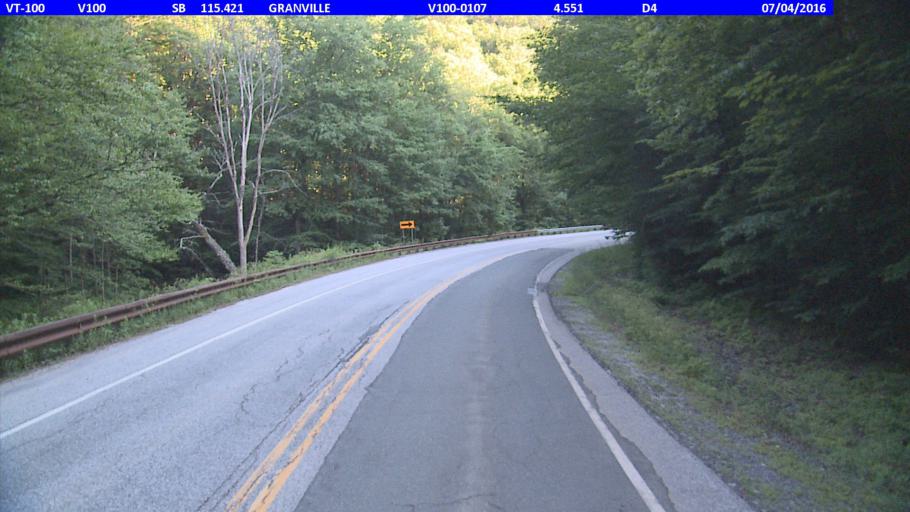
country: US
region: Vermont
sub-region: Orange County
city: Randolph
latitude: 44.0045
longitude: -72.8490
